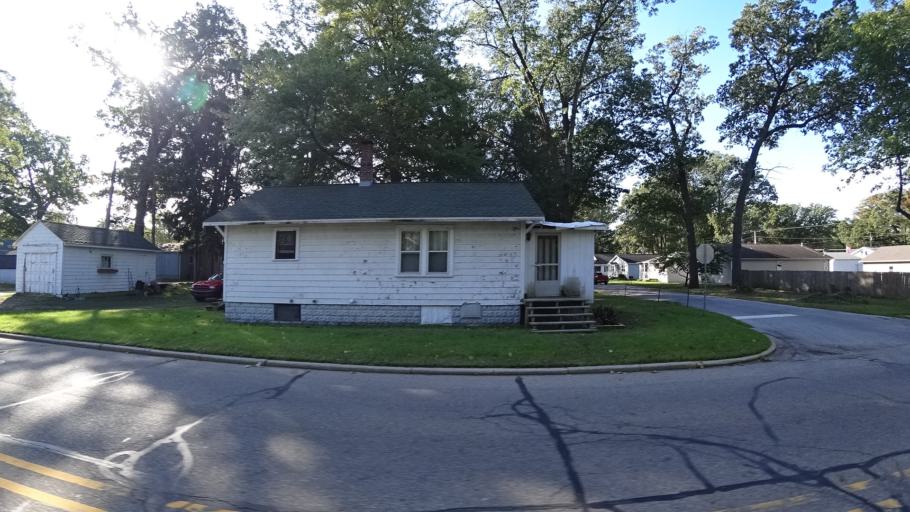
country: US
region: Indiana
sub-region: LaPorte County
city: Trail Creek
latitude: 41.7058
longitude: -86.8704
